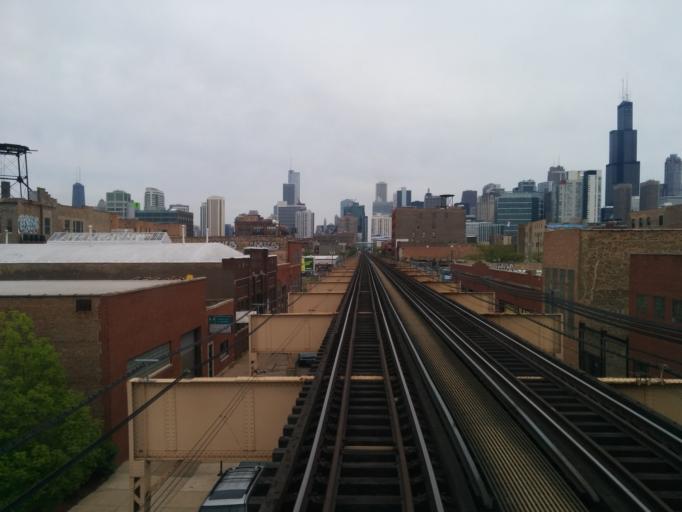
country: US
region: Illinois
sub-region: Cook County
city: Chicago
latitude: 41.8856
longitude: -87.6579
